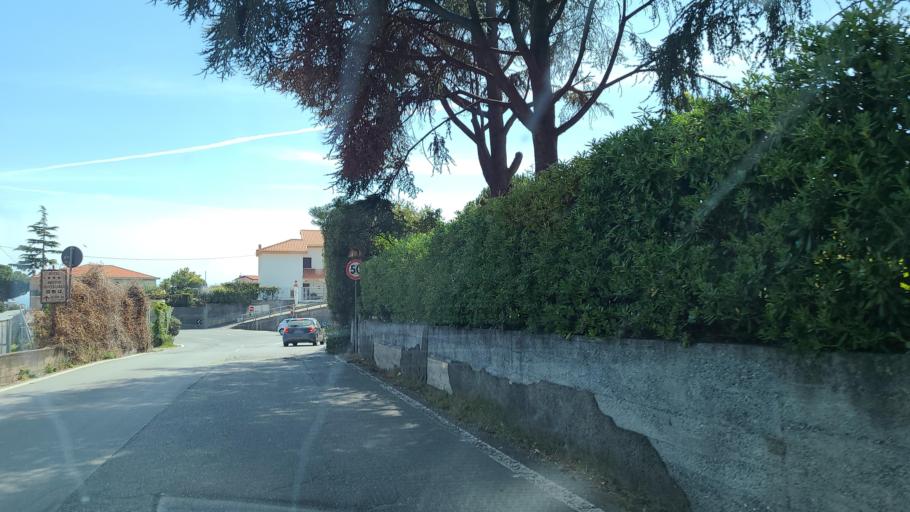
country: IT
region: Liguria
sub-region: Provincia di Imperia
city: Taggia
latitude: 43.8414
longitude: 7.8437
